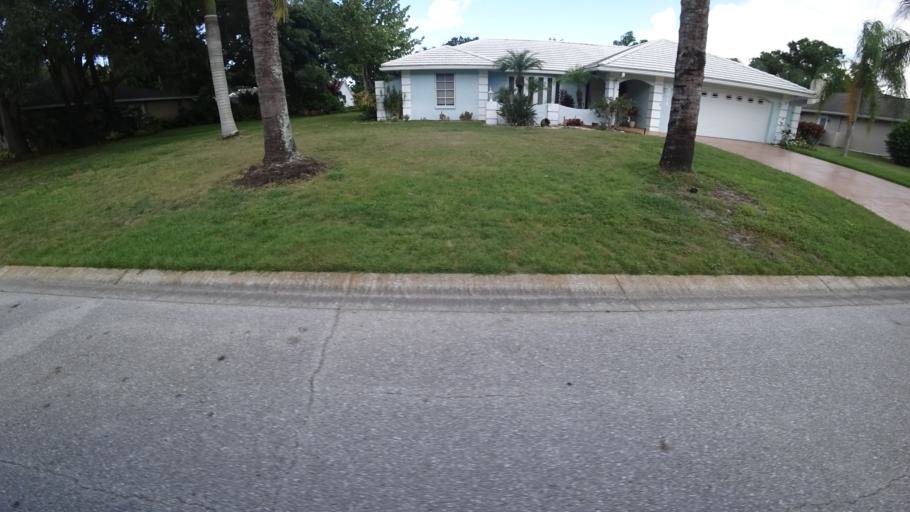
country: US
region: Florida
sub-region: Sarasota County
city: Desoto Lakes
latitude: 27.3972
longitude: -82.4937
